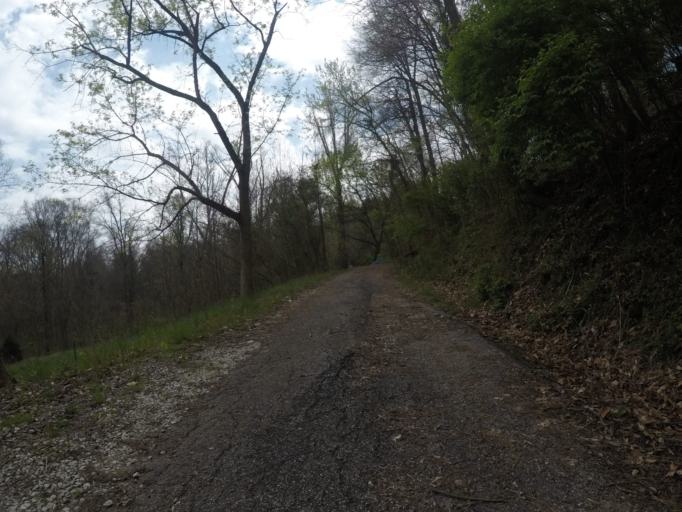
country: US
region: Ohio
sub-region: Lawrence County
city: Burlington
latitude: 38.3900
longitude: -82.5128
